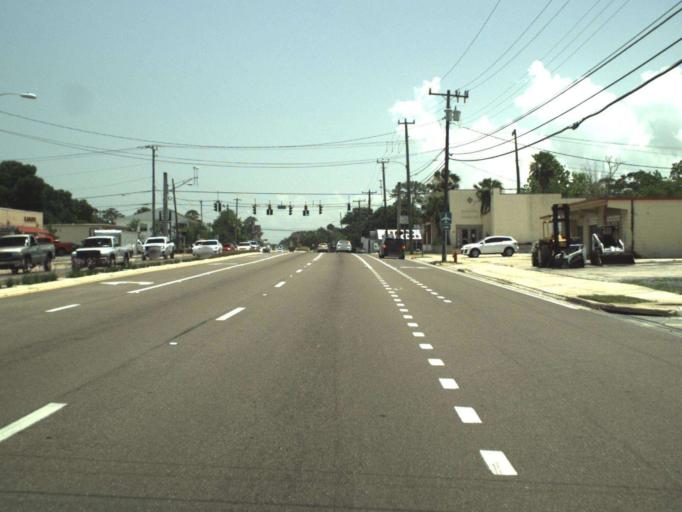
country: US
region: Florida
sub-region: Volusia County
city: Edgewater
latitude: 28.9926
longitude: -80.9085
